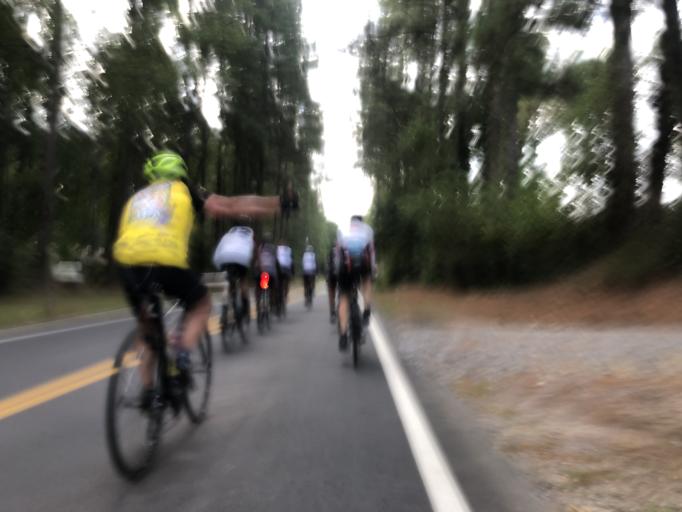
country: US
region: Georgia
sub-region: Fulton County
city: Palmetto
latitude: 33.6079
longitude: -84.6619
